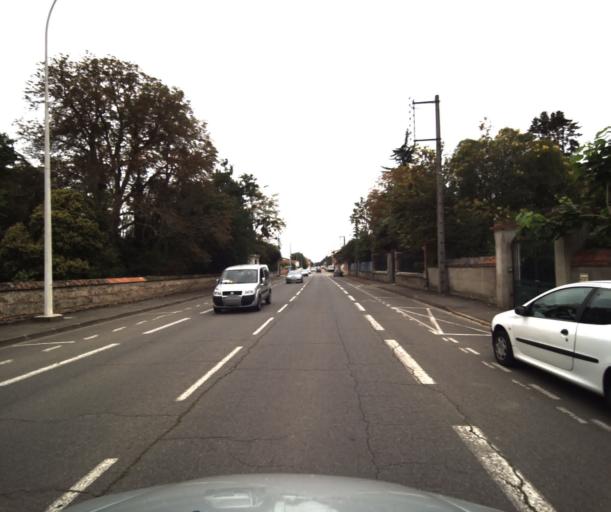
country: FR
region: Midi-Pyrenees
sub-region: Departement de la Haute-Garonne
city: Muret
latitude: 43.4559
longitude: 1.3231
